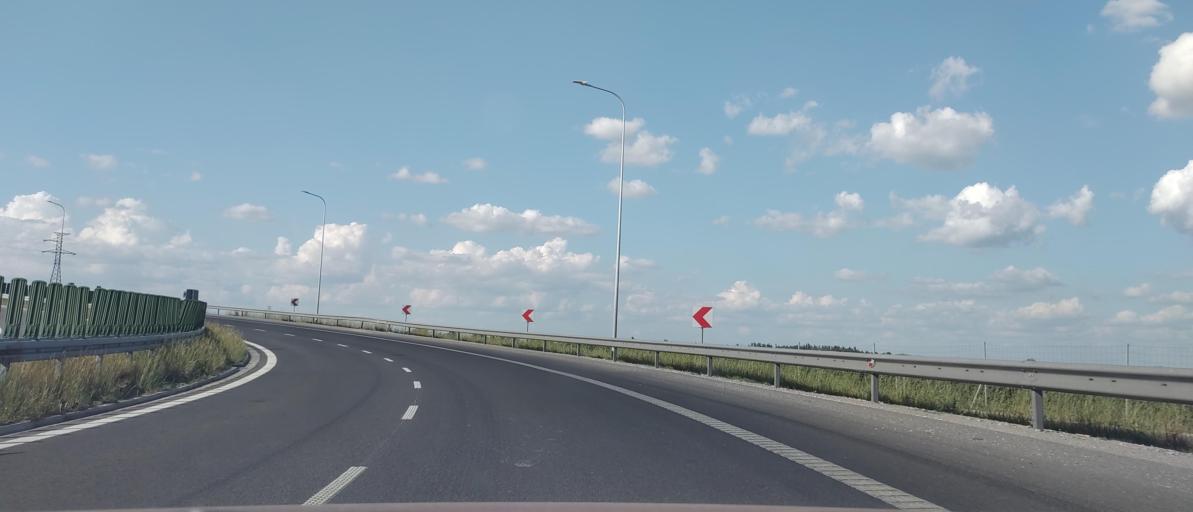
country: PL
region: Masovian Voivodeship
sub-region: Powiat piaseczynski
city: Tarczyn
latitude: 51.9499
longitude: 20.8472
